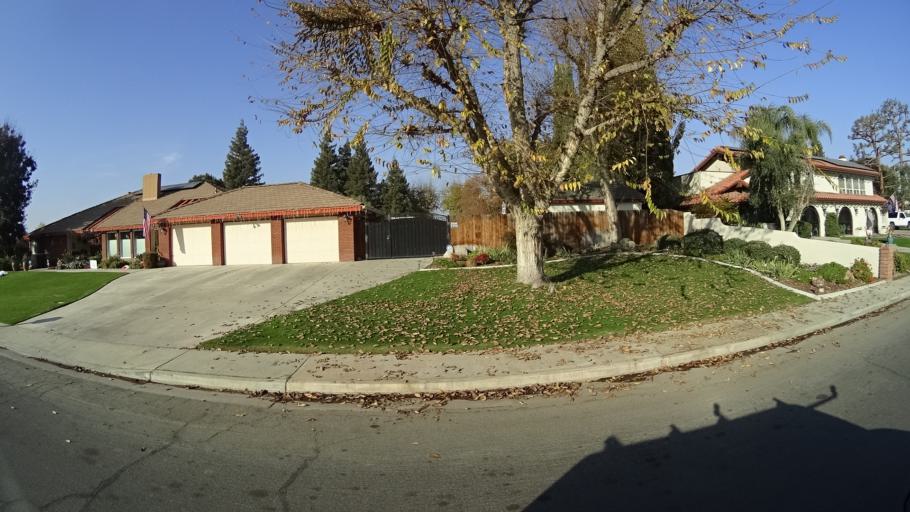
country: US
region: California
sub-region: Kern County
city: Rosedale
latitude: 35.3582
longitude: -119.1500
